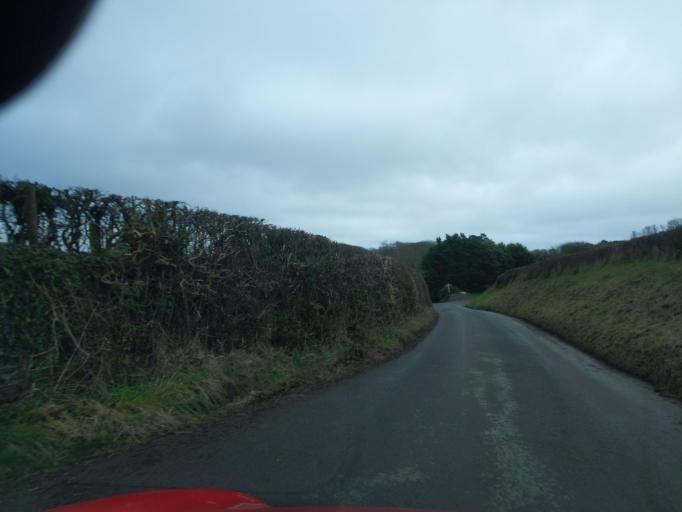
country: GB
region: England
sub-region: Devon
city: Wembury
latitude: 50.3291
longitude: -4.0926
